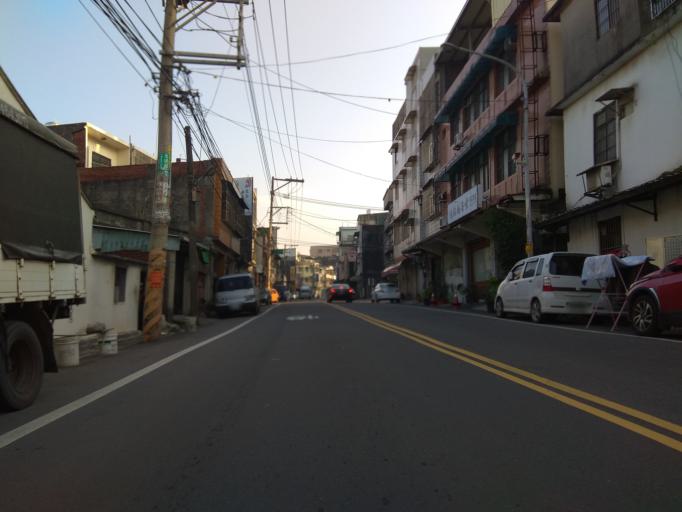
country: TW
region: Taiwan
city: Daxi
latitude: 24.9194
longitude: 121.1857
